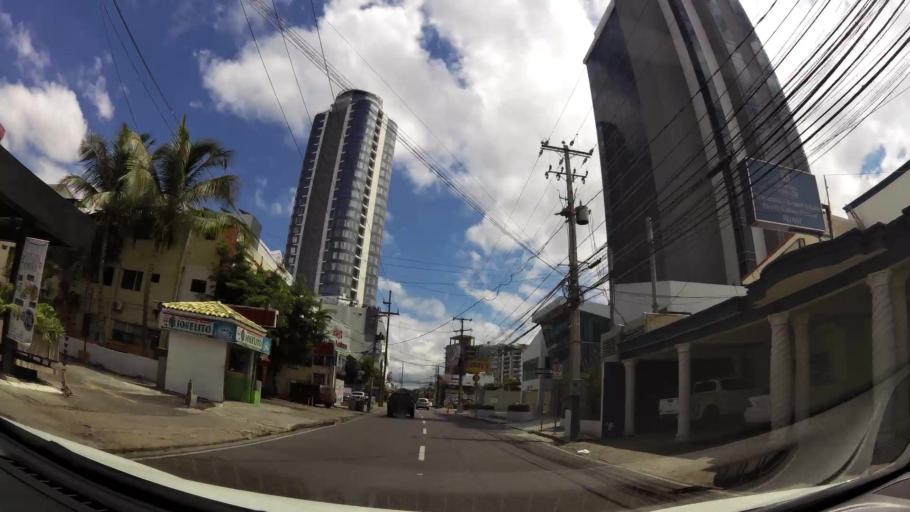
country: DO
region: Nacional
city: La Julia
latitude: 18.4754
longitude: -69.9288
